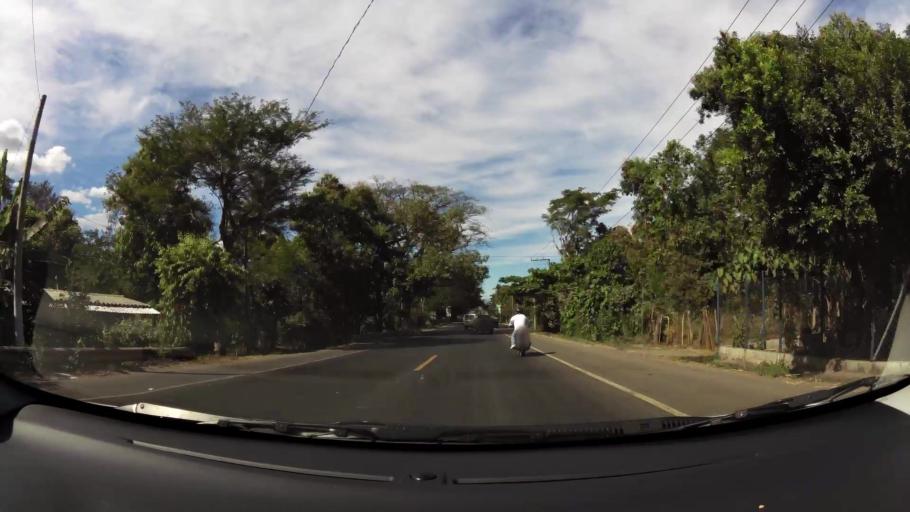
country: SV
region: San Salvador
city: Aguilares
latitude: 13.9252
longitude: -89.1851
